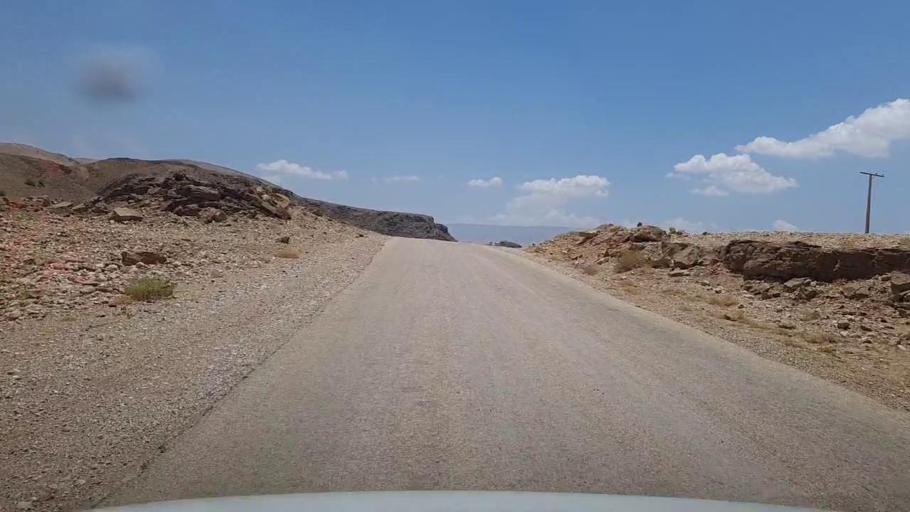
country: PK
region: Sindh
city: Bhan
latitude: 26.3140
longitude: 67.5425
